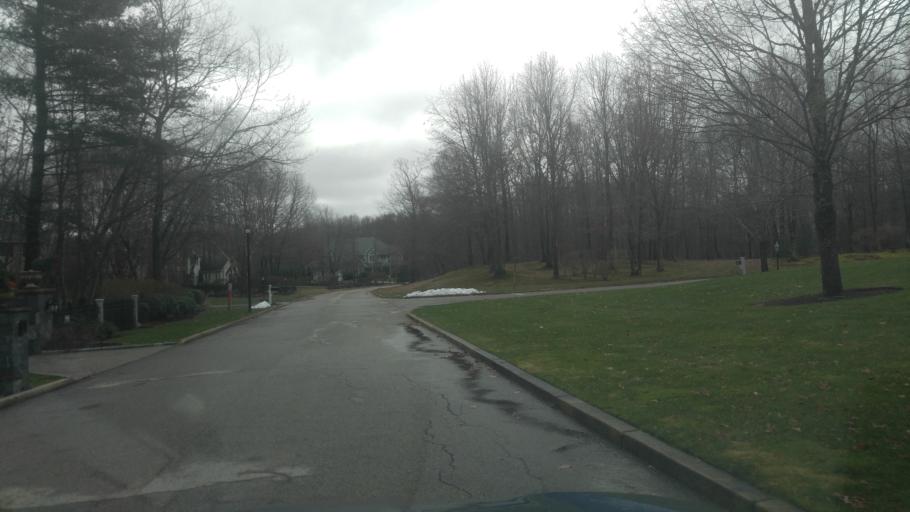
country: US
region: Rhode Island
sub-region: Kent County
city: West Warwick
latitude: 41.6485
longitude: -71.5373
